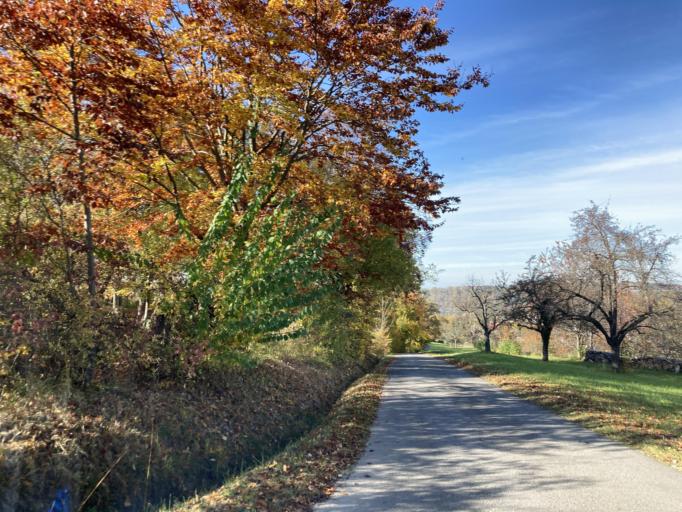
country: DE
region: Baden-Wuerttemberg
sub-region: Tuebingen Region
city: Gomaringen
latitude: 48.4105
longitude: 9.1162
